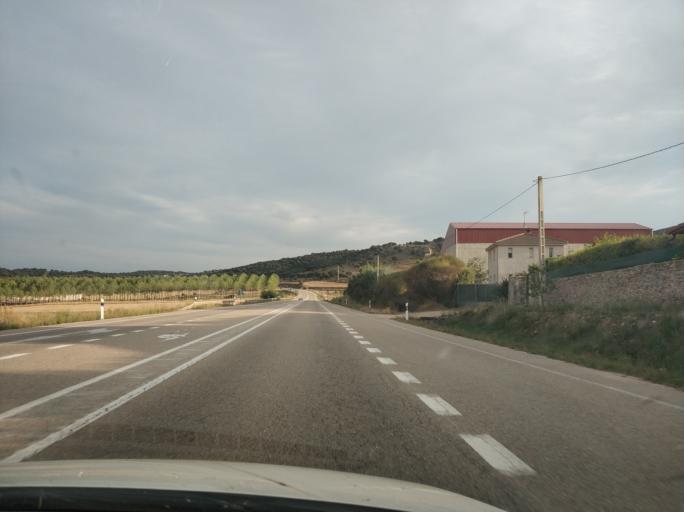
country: ES
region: Castille and Leon
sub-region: Provincia de Burgos
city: Hontoria de la Cantera
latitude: 42.1892
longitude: -3.6409
